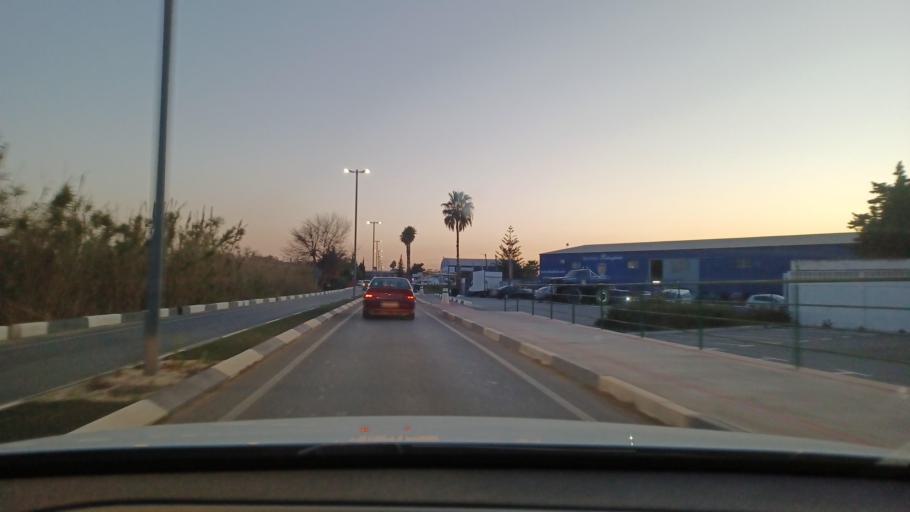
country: ES
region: Valencia
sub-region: Provincia de Alicante
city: Dolores
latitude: 38.1295
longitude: -0.7773
